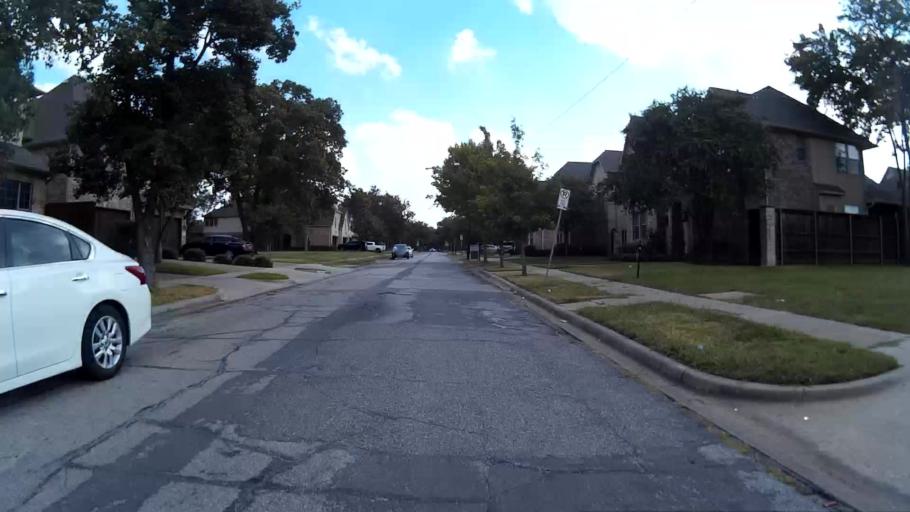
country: US
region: Texas
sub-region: Dallas County
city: Highland Park
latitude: 32.8212
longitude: -96.7838
